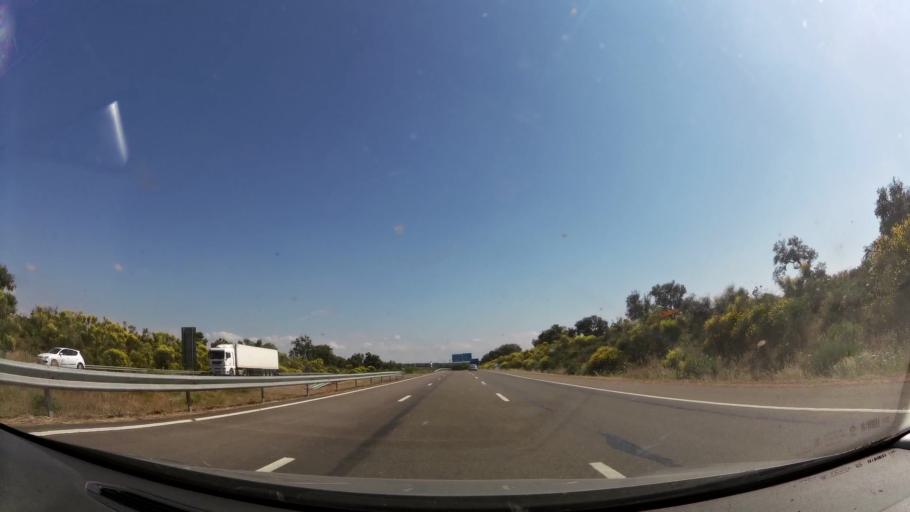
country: MA
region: Rabat-Sale-Zemmour-Zaer
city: Sale
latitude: 34.0365
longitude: -6.7120
